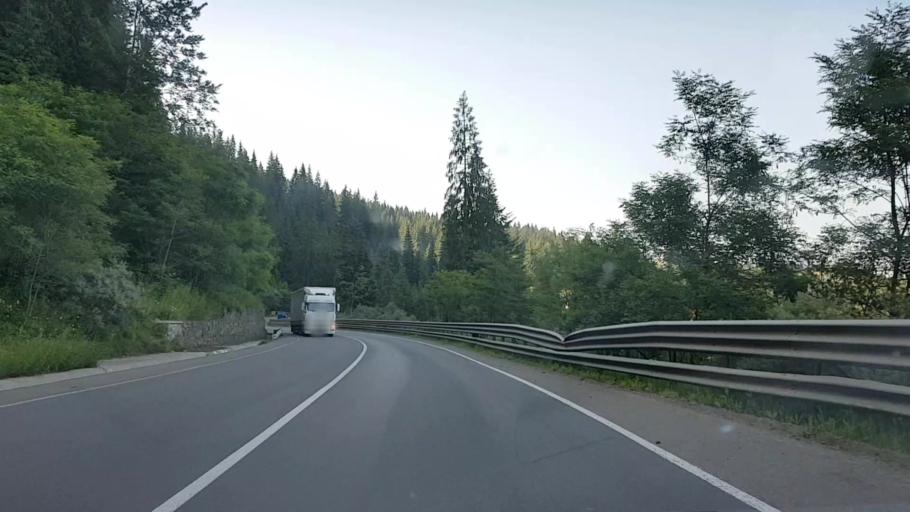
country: RO
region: Bistrita-Nasaud
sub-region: Comuna Lunca Ilvei
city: Lunca Ilvei
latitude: 47.2289
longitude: 24.9635
